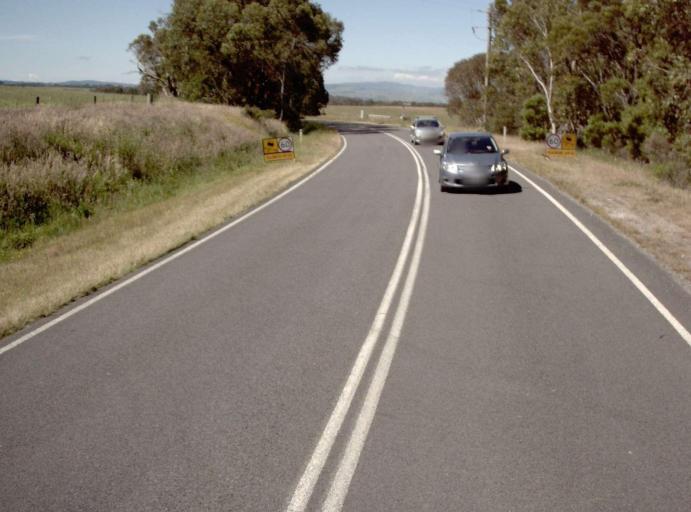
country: AU
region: Victoria
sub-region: Bass Coast
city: North Wonthaggi
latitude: -38.7439
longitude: 146.1420
